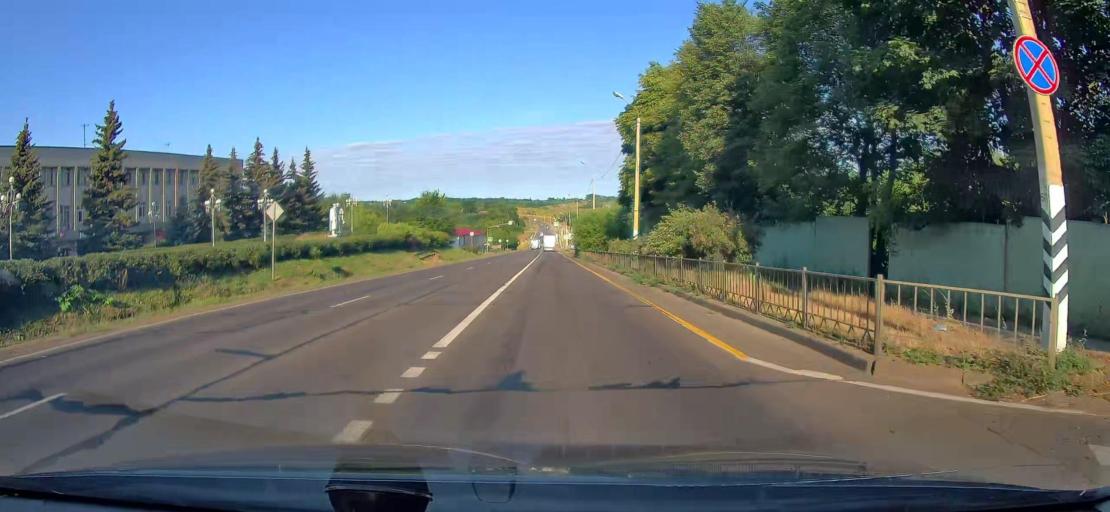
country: RU
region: Tula
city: Chern'
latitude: 53.4547
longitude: 36.9098
